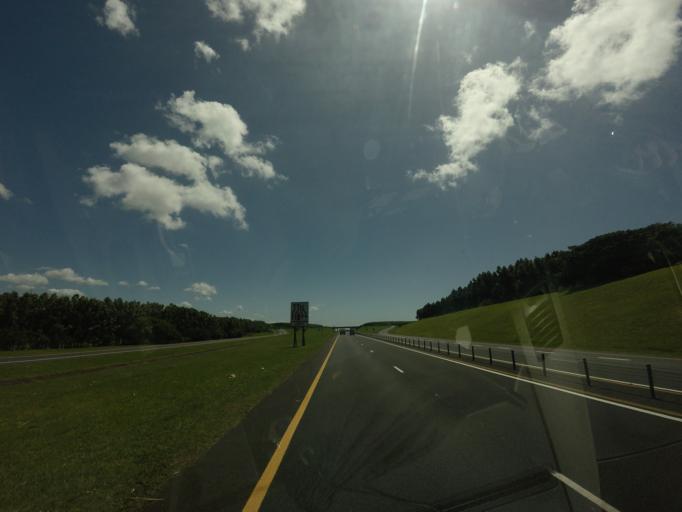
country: ZA
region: KwaZulu-Natal
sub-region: uThungulu District Municipality
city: Eshowe
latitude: -29.0445
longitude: 31.6449
